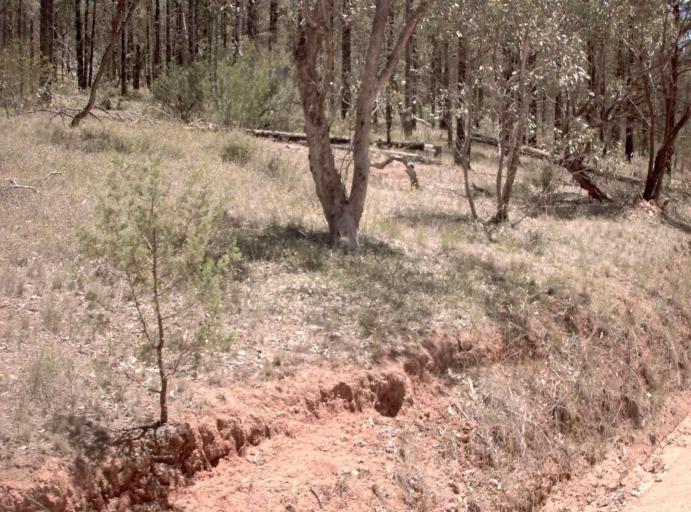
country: AU
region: New South Wales
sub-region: Snowy River
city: Jindabyne
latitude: -36.8936
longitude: 148.4228
